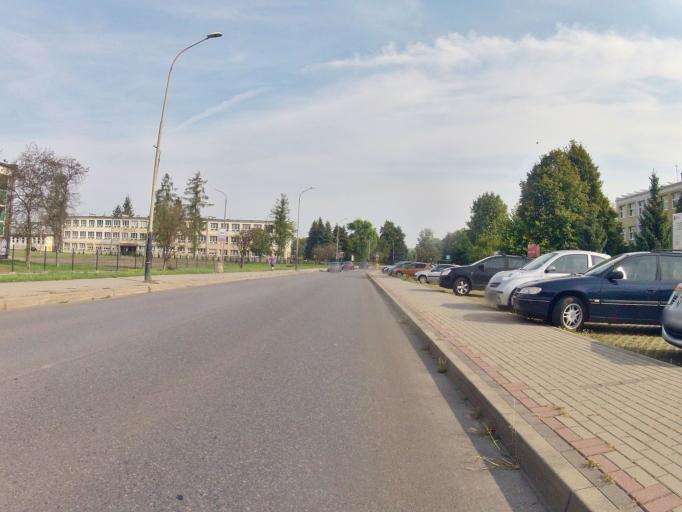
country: PL
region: Subcarpathian Voivodeship
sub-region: Powiat jasielski
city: Jaslo
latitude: 49.7463
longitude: 21.4609
